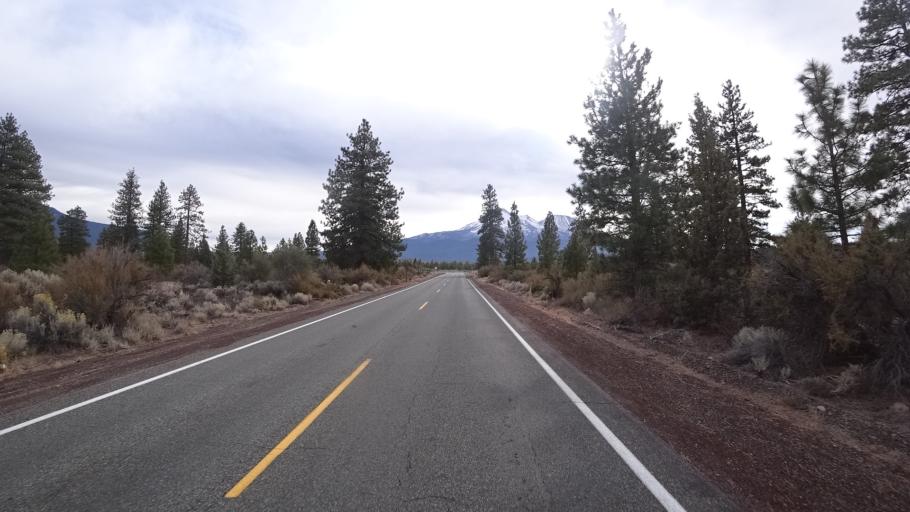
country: US
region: California
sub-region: Siskiyou County
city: Weed
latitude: 41.5368
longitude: -122.2435
